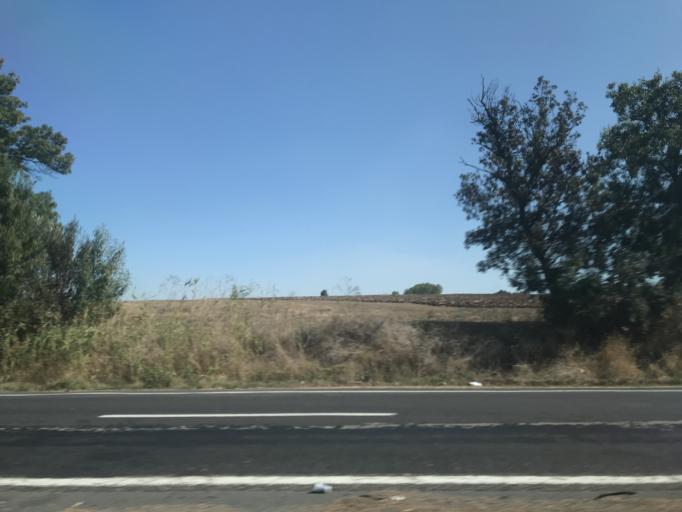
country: TR
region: Tekirdag
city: Muratli
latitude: 41.1323
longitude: 27.4887
